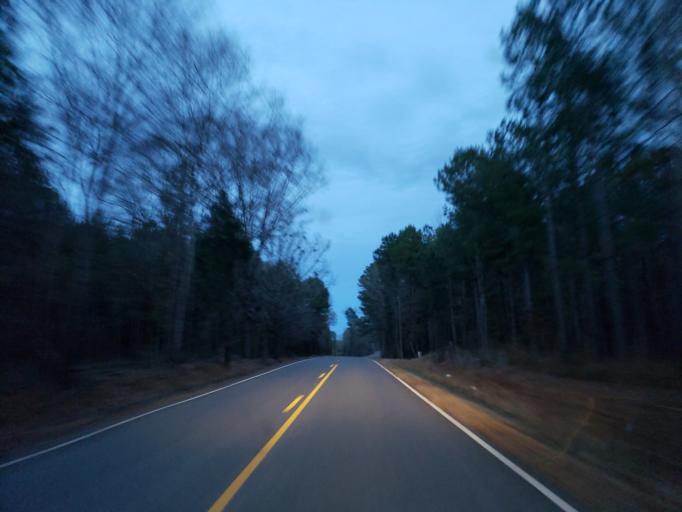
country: US
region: Alabama
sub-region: Greene County
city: Eutaw
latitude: 32.8844
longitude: -88.0579
